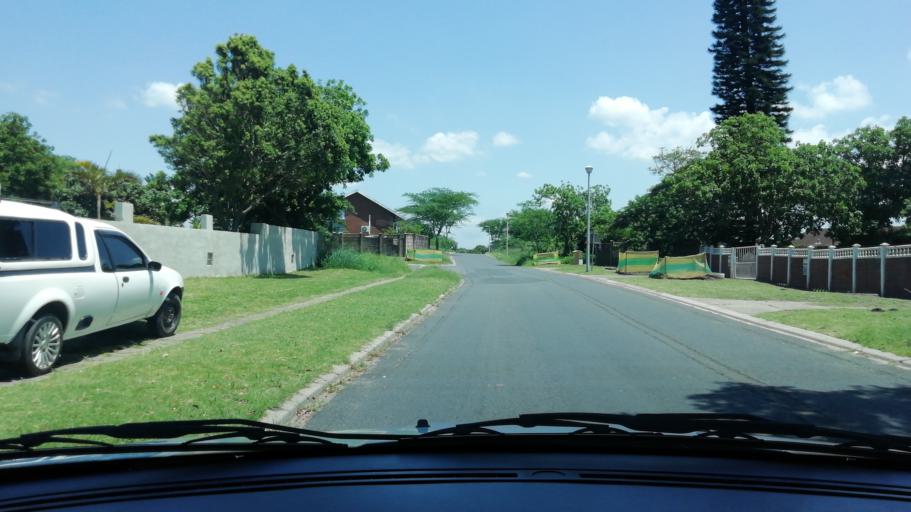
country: ZA
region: KwaZulu-Natal
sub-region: uThungulu District Municipality
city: Richards Bay
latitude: -28.7369
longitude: 32.0534
